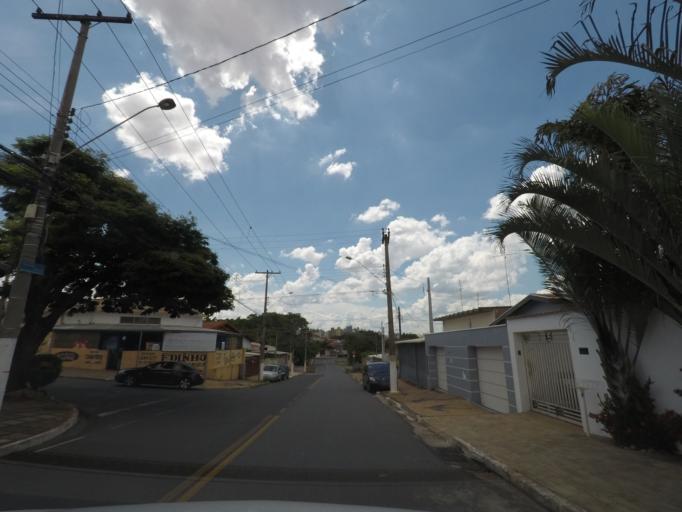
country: BR
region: Sao Paulo
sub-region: Campinas
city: Campinas
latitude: -22.9183
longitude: -47.0345
